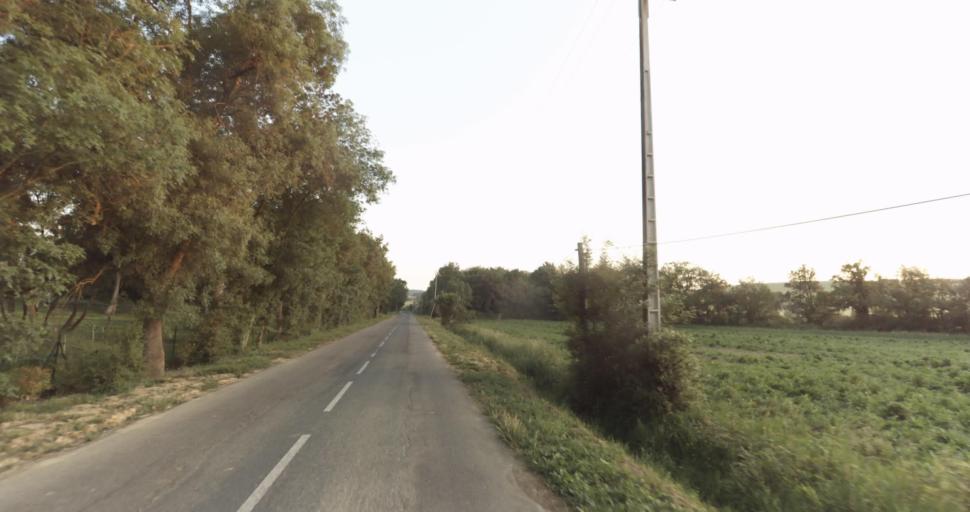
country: FR
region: Midi-Pyrenees
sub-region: Departement du Gers
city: Pujaudran
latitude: 43.6495
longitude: 1.1361
